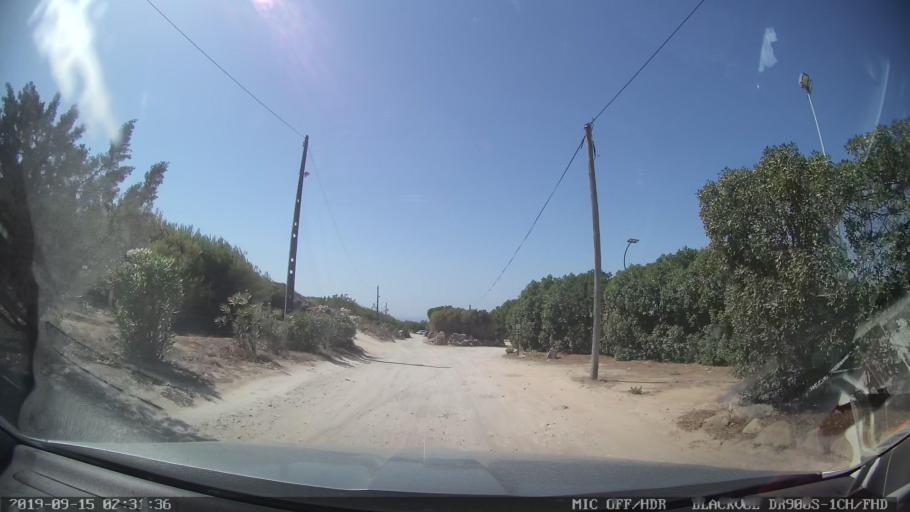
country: PT
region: Lisbon
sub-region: Cascais
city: Cascais
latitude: 38.7207
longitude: -9.4698
